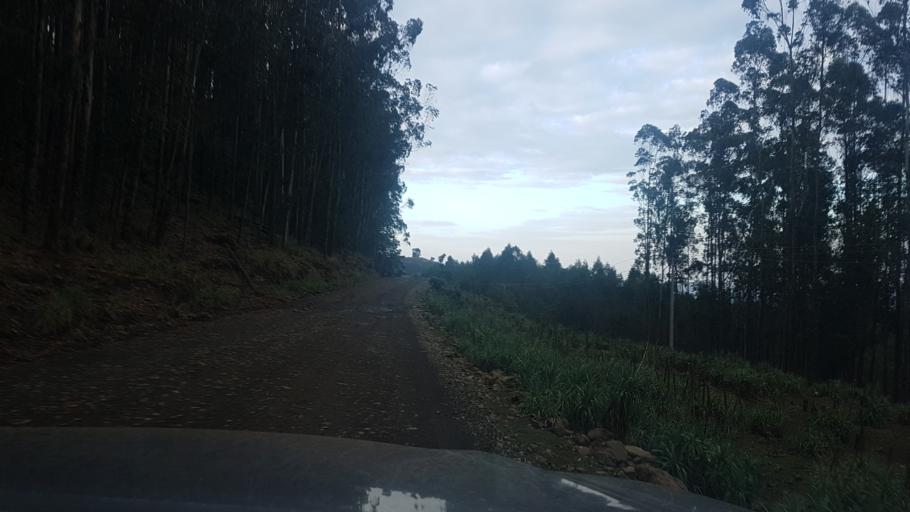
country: ET
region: Amhara
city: Finote Selam
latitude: 10.7923
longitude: 37.6641
